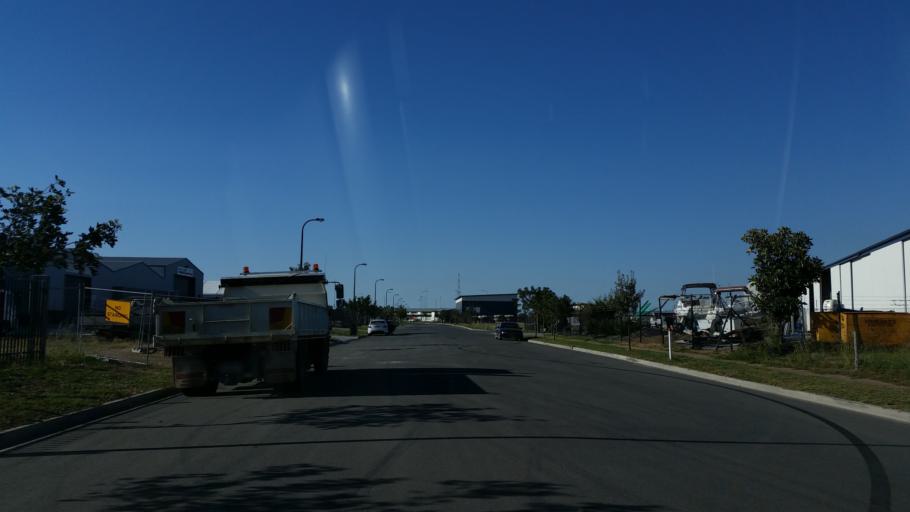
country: AU
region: South Australia
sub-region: Port Adelaide Enfield
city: Birkenhead
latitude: -34.8205
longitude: 138.5082
